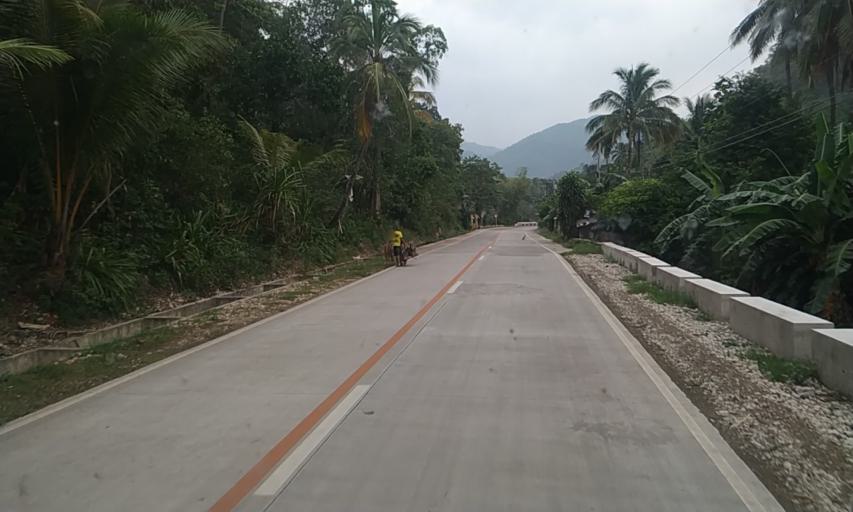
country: PH
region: Central Visayas
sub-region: Province of Negros Oriental
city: Calamba
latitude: 10.1950
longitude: 123.2951
